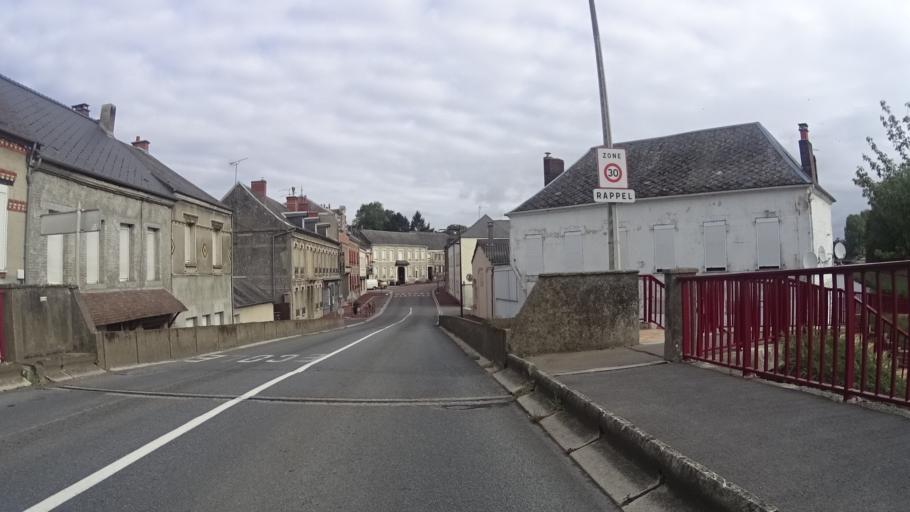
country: FR
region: Picardie
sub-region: Departement de l'Aisne
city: Etreux
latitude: 49.9912
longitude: 3.6548
